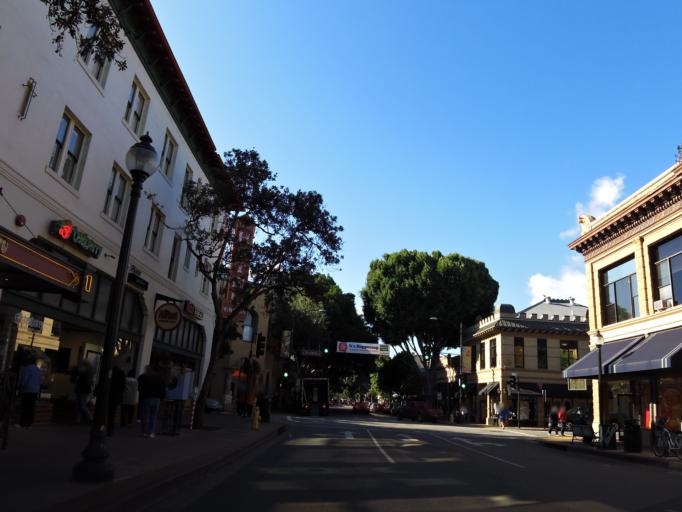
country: US
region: California
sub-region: San Luis Obispo County
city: San Luis Obispo
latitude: 35.2801
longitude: -120.6626
